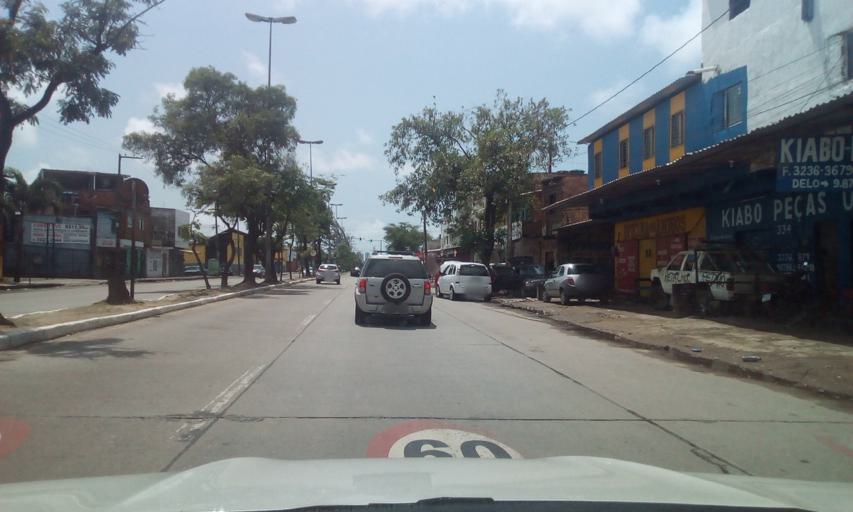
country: BR
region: Pernambuco
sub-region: Recife
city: Recife
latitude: -8.0647
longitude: -34.9370
